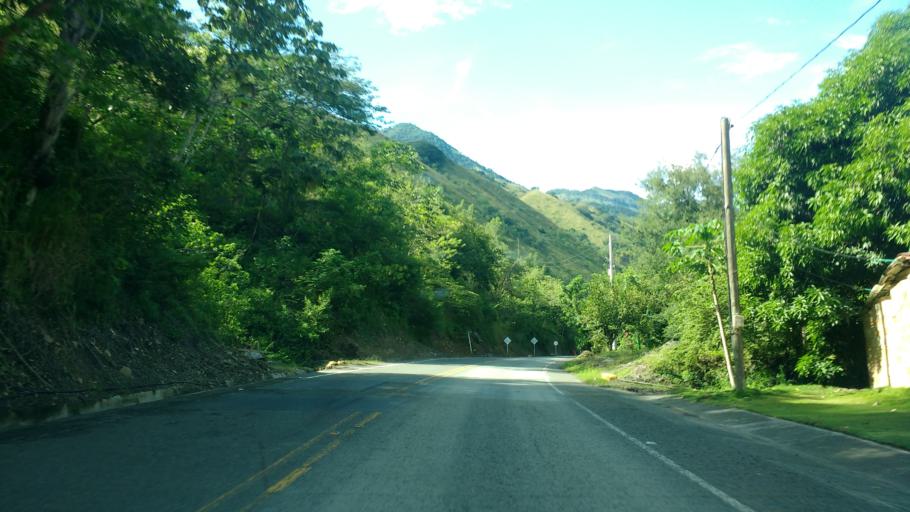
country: CO
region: Antioquia
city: Concordia
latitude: 6.0419
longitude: -75.8629
